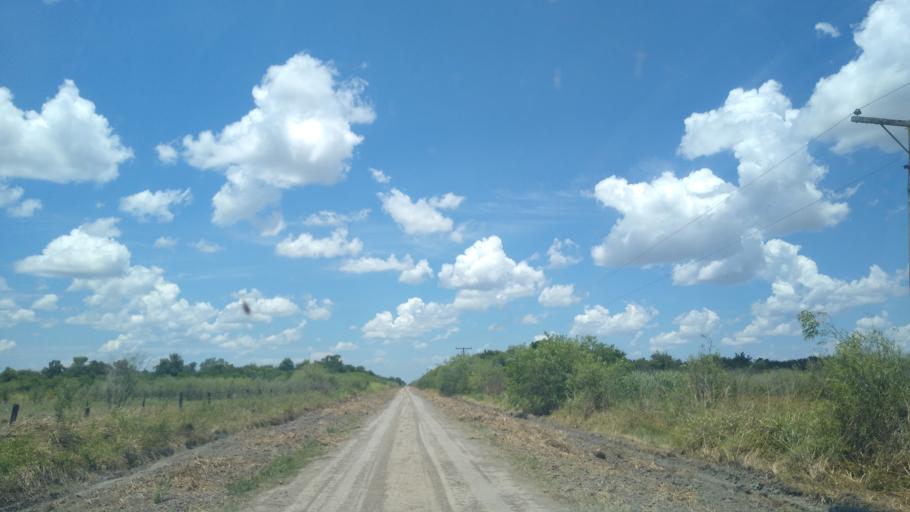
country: AR
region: Chaco
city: Presidencia Roque Saenz Pena
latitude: -26.7377
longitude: -60.3320
